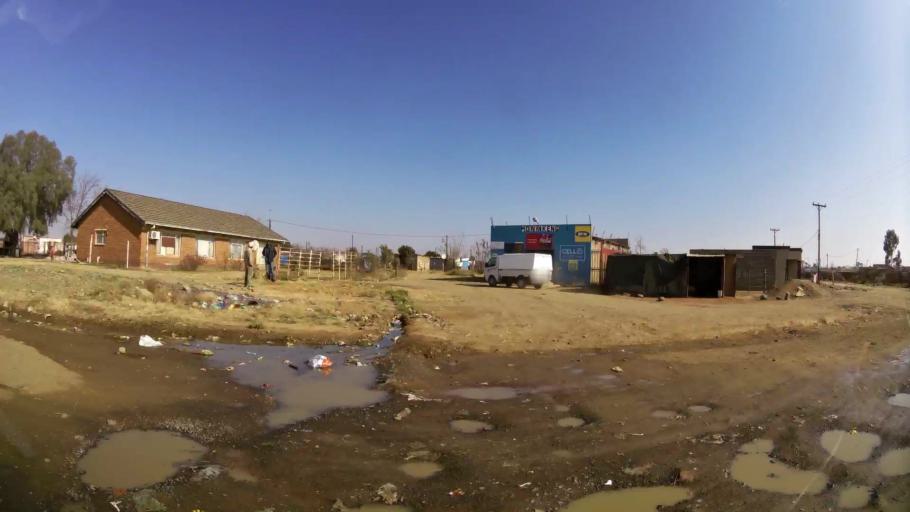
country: ZA
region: Orange Free State
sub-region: Mangaung Metropolitan Municipality
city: Bloemfontein
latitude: -29.1741
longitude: 26.2908
